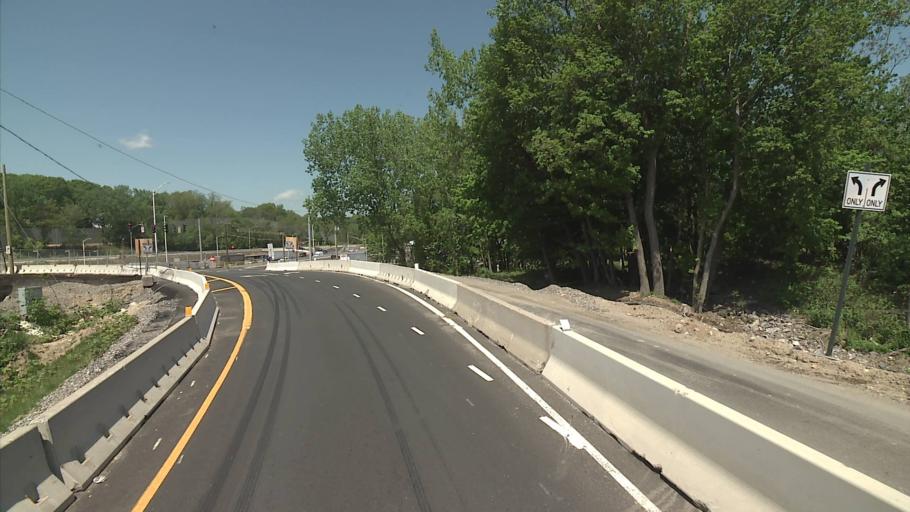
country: US
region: Connecticut
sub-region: New Haven County
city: Waterbury
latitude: 41.5428
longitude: -73.0227
